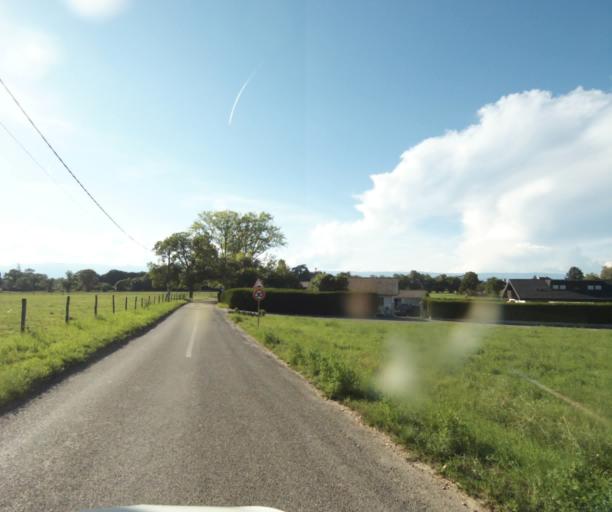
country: FR
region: Rhone-Alpes
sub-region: Departement de la Haute-Savoie
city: Douvaine
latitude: 46.2996
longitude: 6.3031
